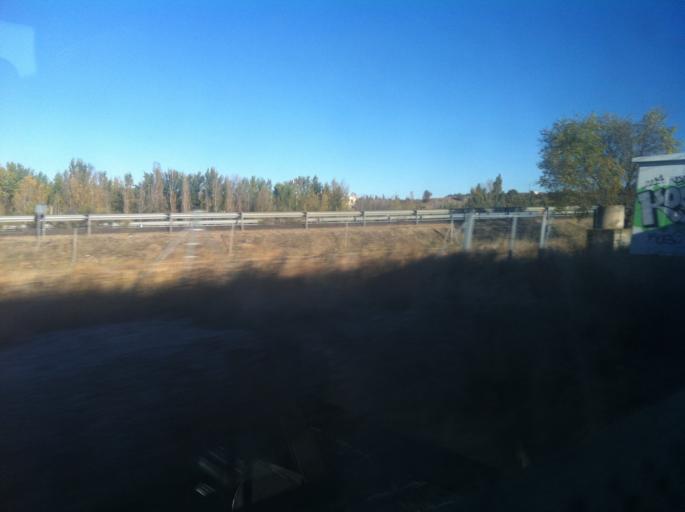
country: ES
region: Castille and Leon
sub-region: Provincia de Palencia
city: Duenas
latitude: 41.8581
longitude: -4.5491
